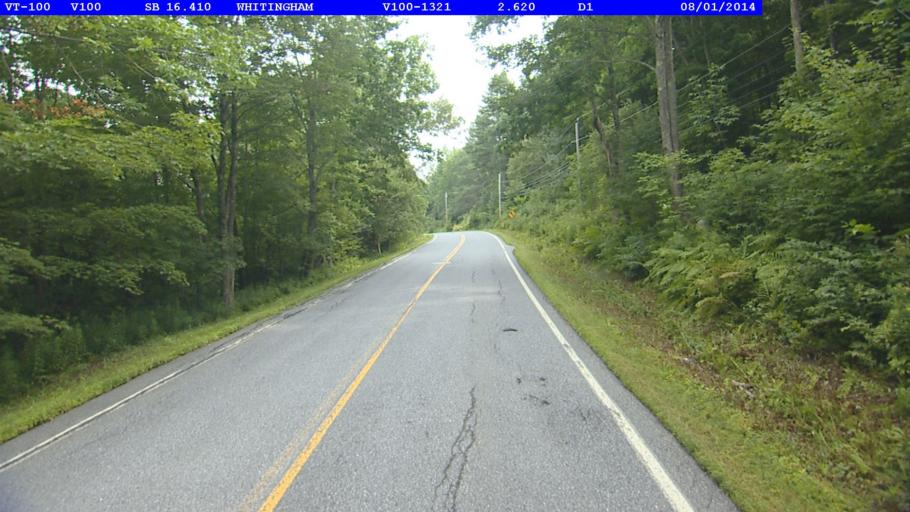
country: US
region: Massachusetts
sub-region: Franklin County
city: Charlemont
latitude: 42.7757
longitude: -72.8955
